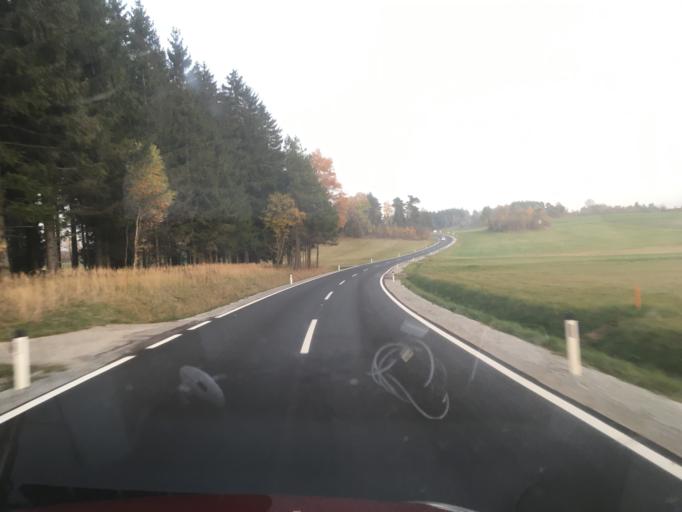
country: AT
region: Lower Austria
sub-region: Politischer Bezirk Zwettl
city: Langschlag
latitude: 48.5693
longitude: 14.9180
